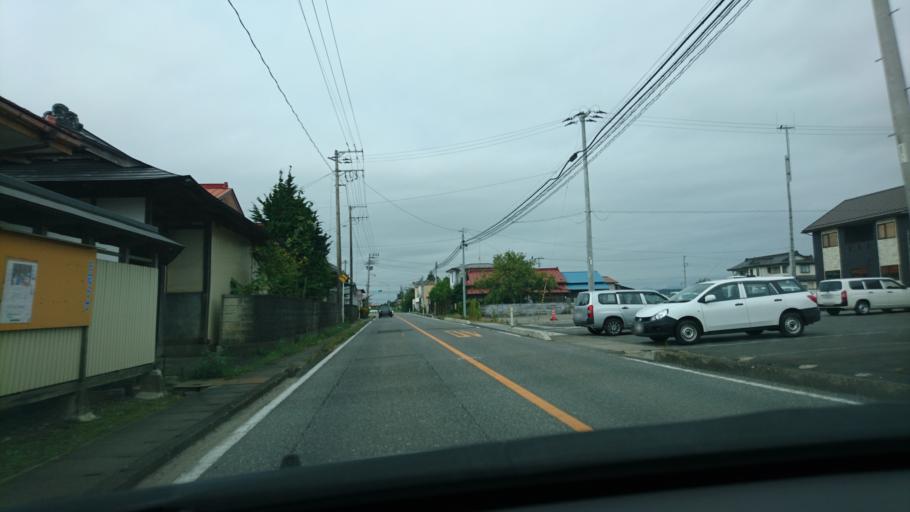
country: JP
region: Iwate
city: Ichinoseki
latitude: 38.7711
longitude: 141.0975
